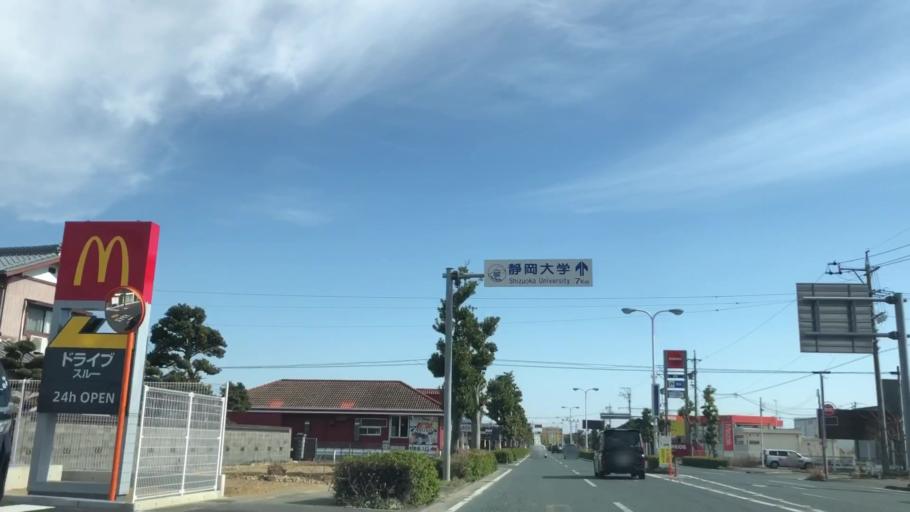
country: JP
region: Shizuoka
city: Hamamatsu
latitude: 34.7618
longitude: 137.6833
